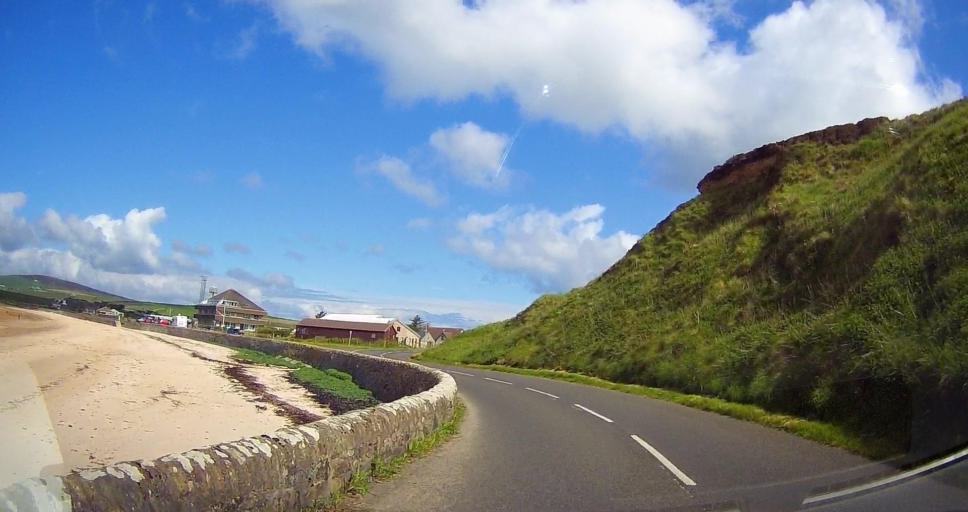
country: GB
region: Scotland
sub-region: Orkney Islands
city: Orkney
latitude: 58.9594
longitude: -2.9685
